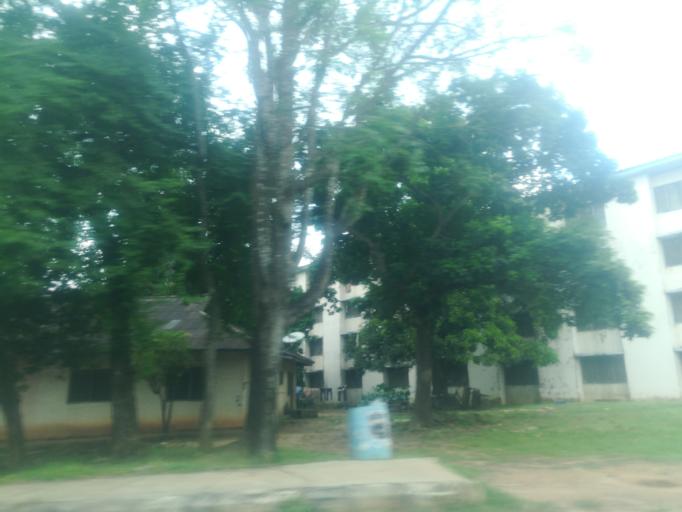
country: NG
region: Oyo
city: Ibadan
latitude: 7.4384
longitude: 3.8969
